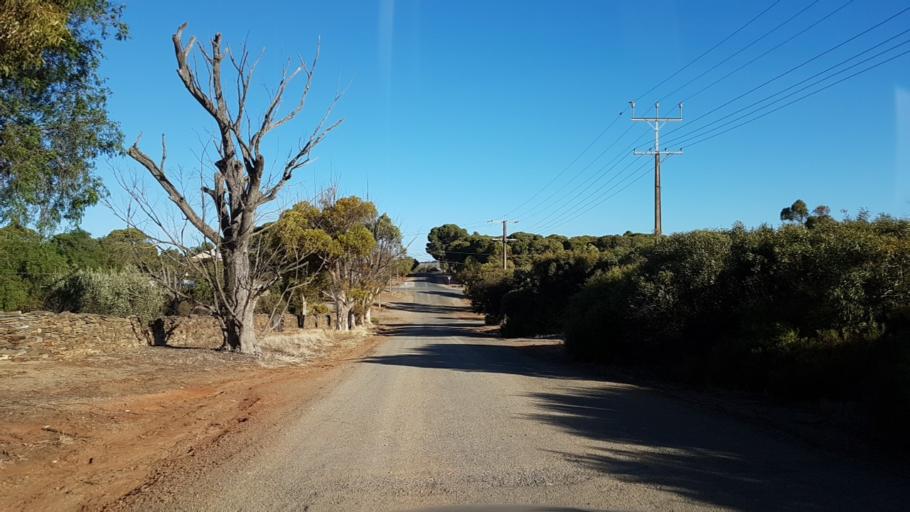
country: AU
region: South Australia
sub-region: Clare and Gilbert Valleys
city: Clare
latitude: -33.6686
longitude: 138.9335
